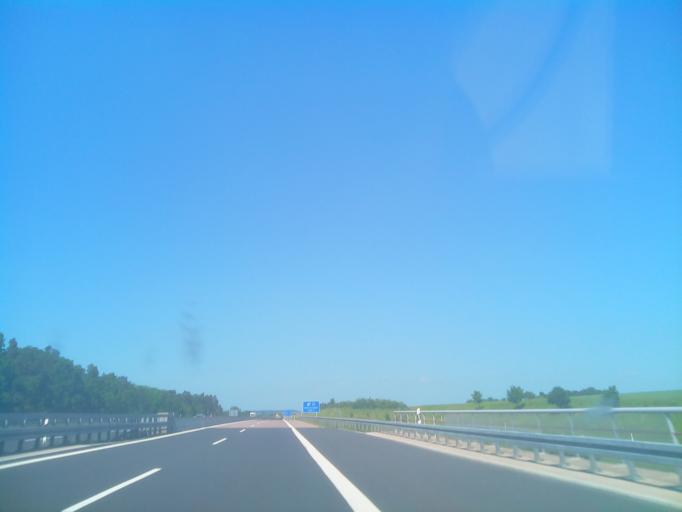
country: DE
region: Bavaria
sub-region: Regierungsbezirk Unterfranken
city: Hendungen
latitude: 50.4021
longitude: 10.3220
